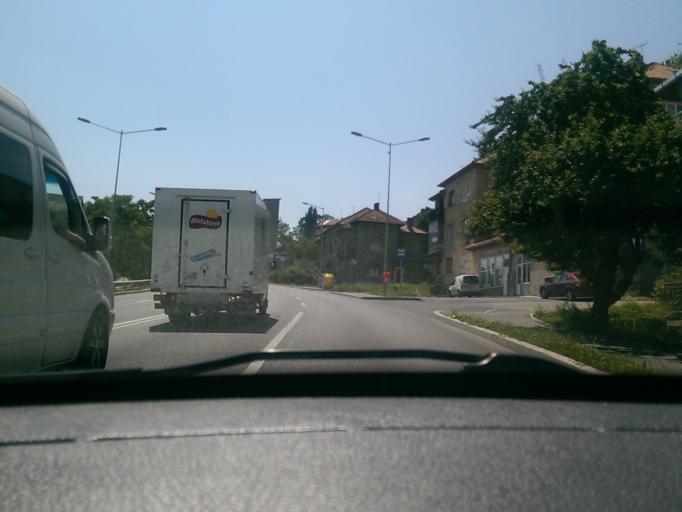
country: RO
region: Cluj
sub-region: Municipiul Cluj-Napoca
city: Cluj-Napoca
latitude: 46.7622
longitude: 23.5977
